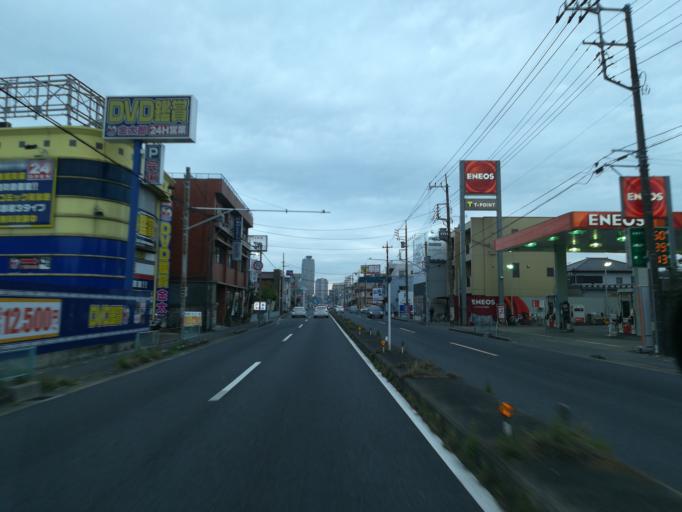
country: JP
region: Saitama
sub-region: Kawaguchi-shi
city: Hatogaya-honcho
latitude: 35.8143
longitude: 139.7356
